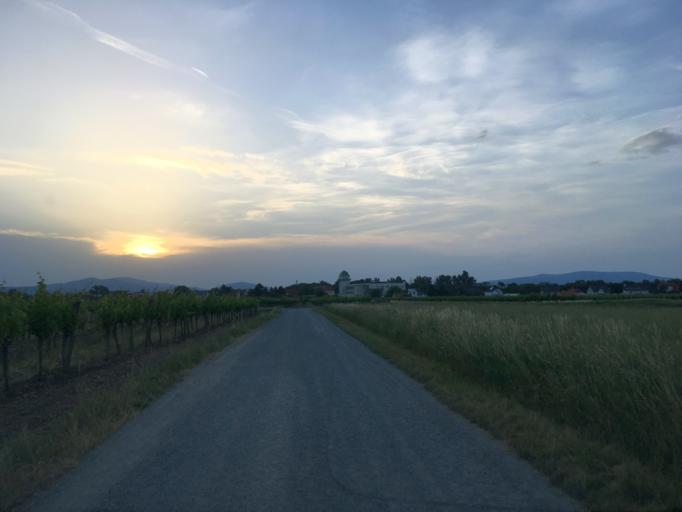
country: AT
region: Lower Austria
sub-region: Politischer Bezirk Baden
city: Tattendorf
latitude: 47.9465
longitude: 16.2919
